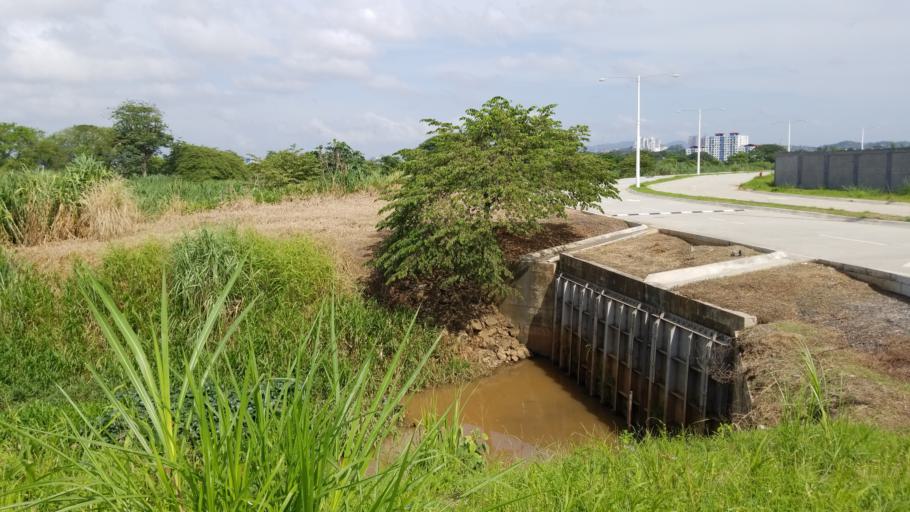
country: PA
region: Panama
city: San Miguelito
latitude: 9.0341
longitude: -79.4467
